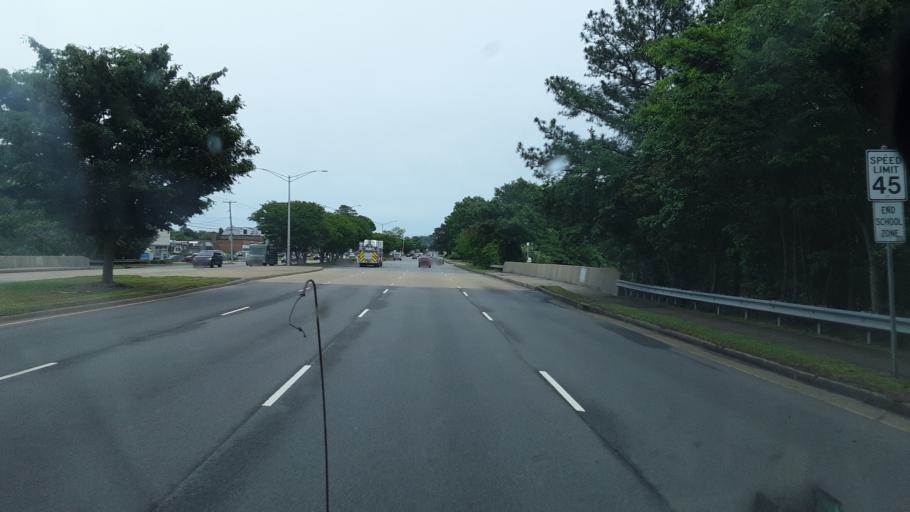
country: US
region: Virginia
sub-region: City of Virginia Beach
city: Virginia Beach
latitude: 36.8433
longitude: -76.1252
